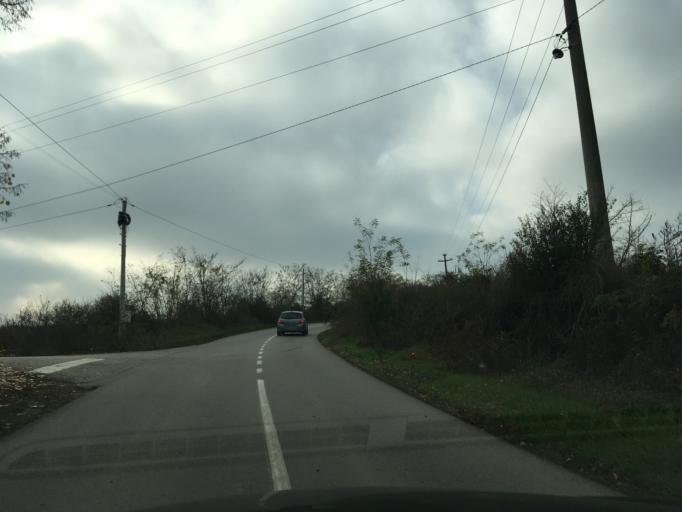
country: RS
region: Central Serbia
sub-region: Belgrade
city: Sopot
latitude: 44.4966
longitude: 20.6217
